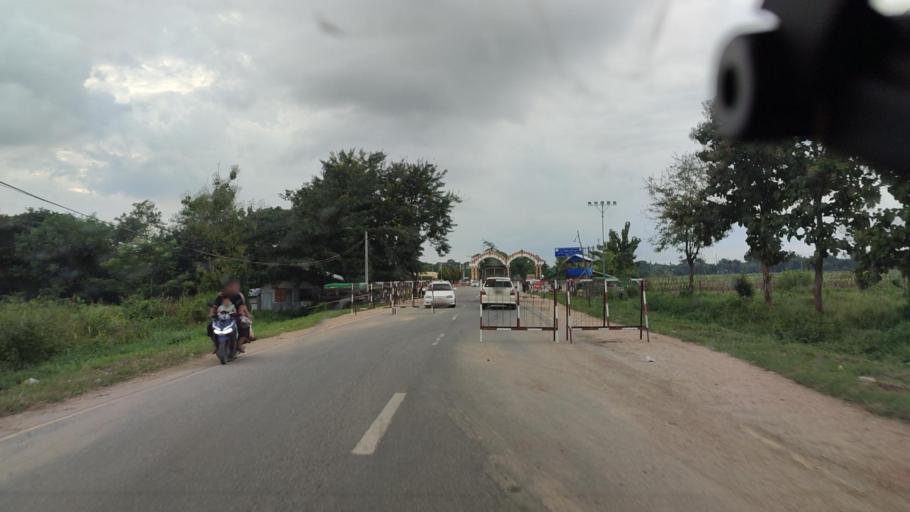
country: MM
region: Bago
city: Pyay
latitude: 18.6869
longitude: 95.2206
